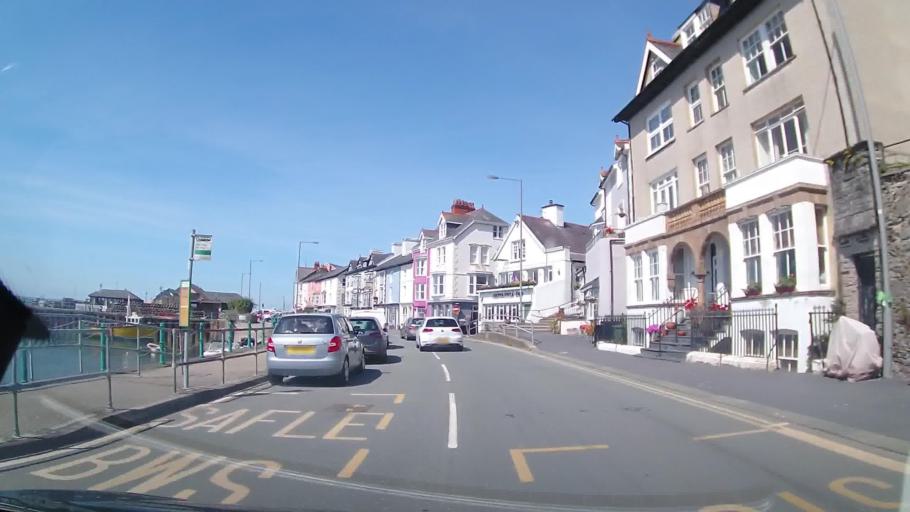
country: GB
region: Wales
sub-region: Gwynedd
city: Tywyn
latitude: 52.5442
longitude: -4.0431
